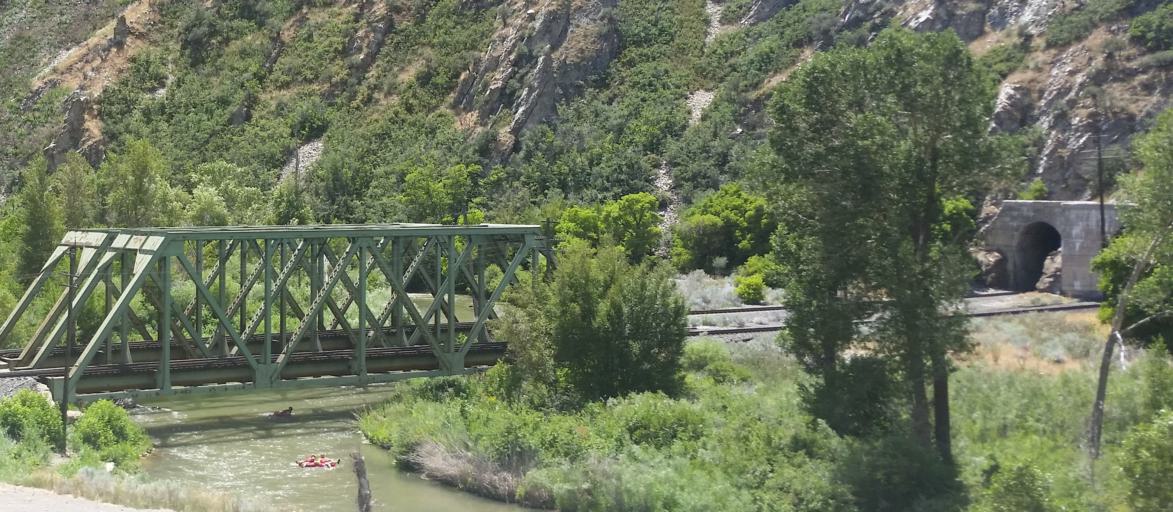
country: US
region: Utah
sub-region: Morgan County
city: Morgan
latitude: 41.0601
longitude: -111.5881
